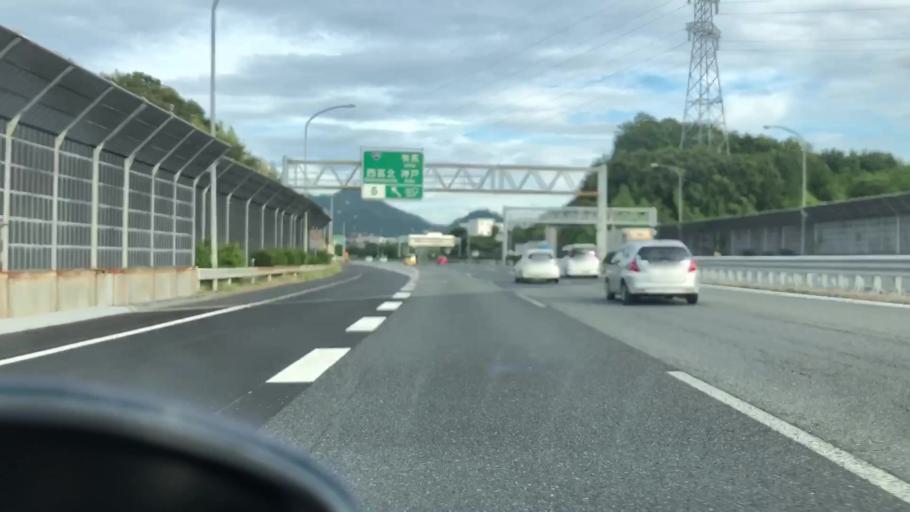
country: JP
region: Hyogo
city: Sandacho
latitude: 34.8400
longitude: 135.2310
